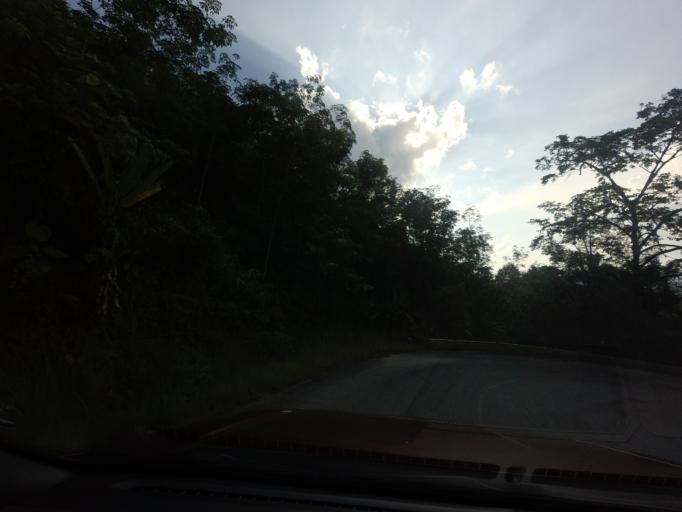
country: TH
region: Yala
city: Than To
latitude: 6.1459
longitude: 101.2829
